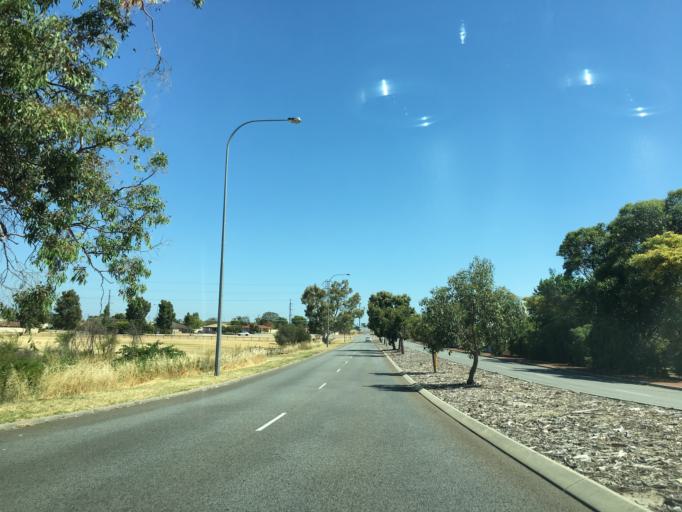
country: AU
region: Western Australia
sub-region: Canning
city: Canning Vale
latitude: -32.0514
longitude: 115.9043
